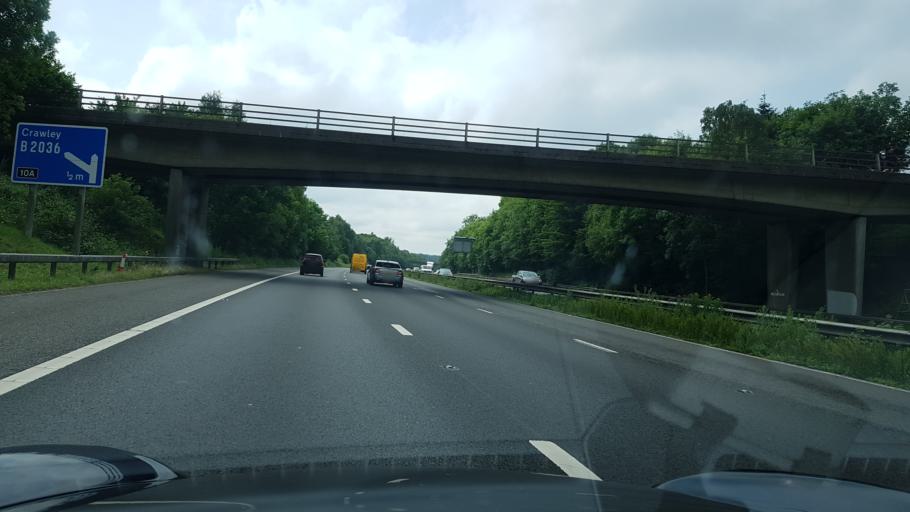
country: GB
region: England
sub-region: West Sussex
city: Maidenbower
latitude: 51.1165
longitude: -0.1372
